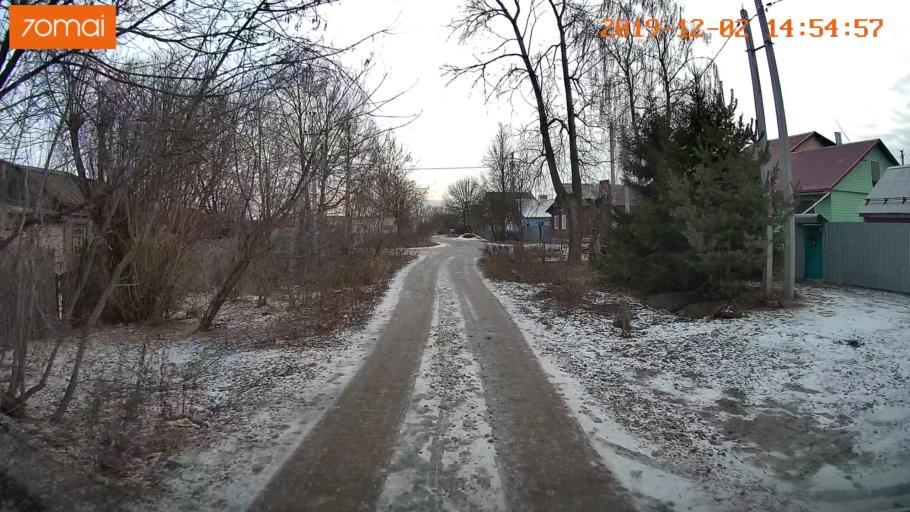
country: RU
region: Ivanovo
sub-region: Gorod Ivanovo
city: Ivanovo
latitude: 56.9743
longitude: 41.0166
